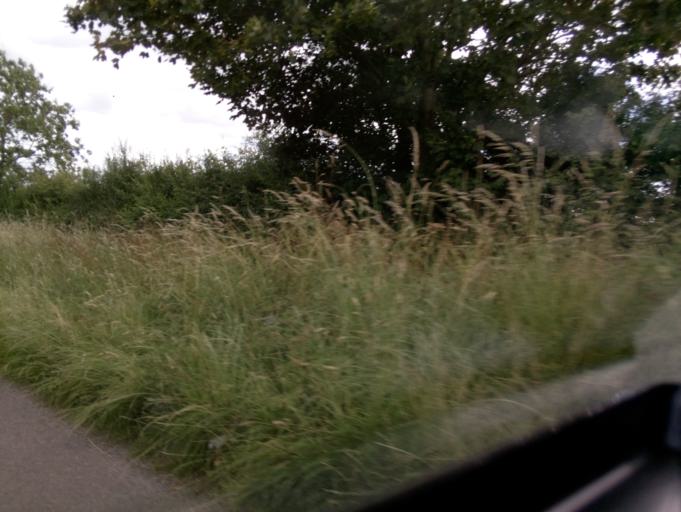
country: GB
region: England
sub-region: Nottinghamshire
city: Cotgrave
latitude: 52.8425
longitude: -1.0816
